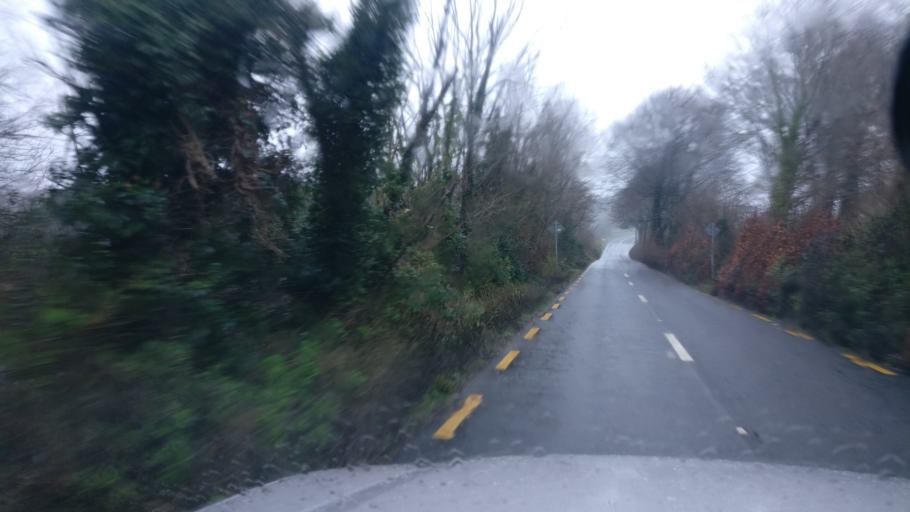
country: IE
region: Connaught
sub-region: County Galway
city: Loughrea
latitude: 53.1370
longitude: -8.4653
